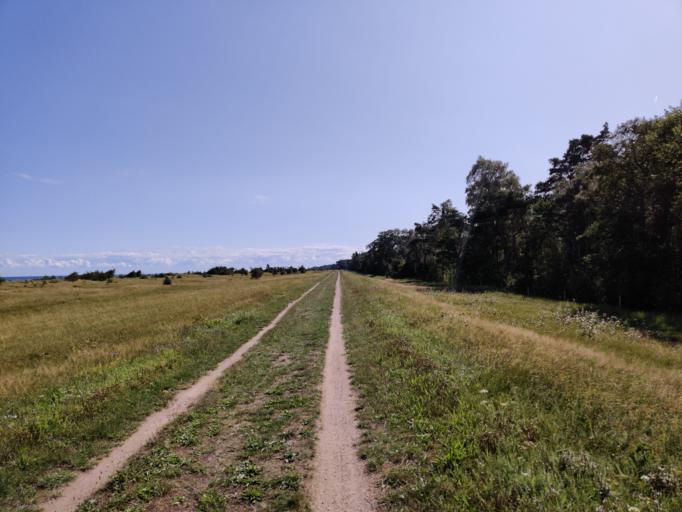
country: DK
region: Zealand
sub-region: Guldborgsund Kommune
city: Nykobing Falster
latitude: 54.6318
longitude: 11.9616
